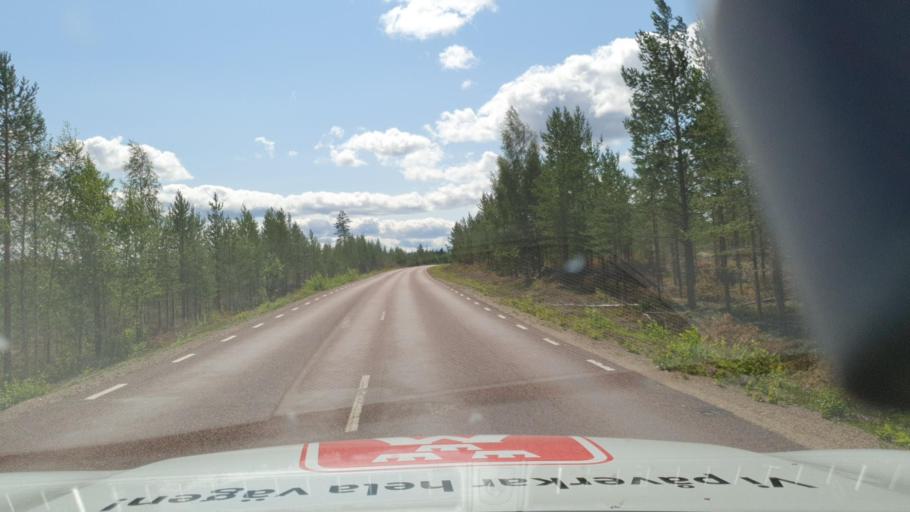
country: SE
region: Jaemtland
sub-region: Harjedalens Kommun
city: Sveg
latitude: 61.9019
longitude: 14.1766
